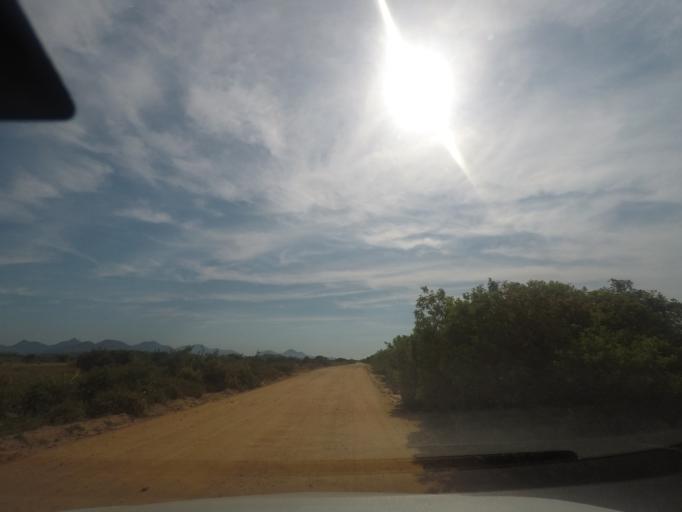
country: BR
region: Rio de Janeiro
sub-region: Marica
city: Marica
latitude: -22.9605
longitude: -42.8515
